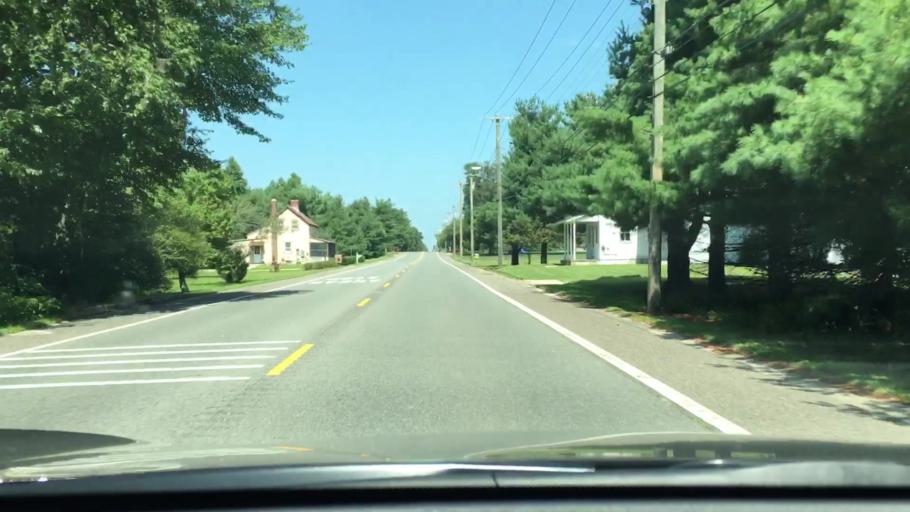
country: US
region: New Jersey
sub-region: Cumberland County
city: Laurel Lake
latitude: 39.2913
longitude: -74.9963
